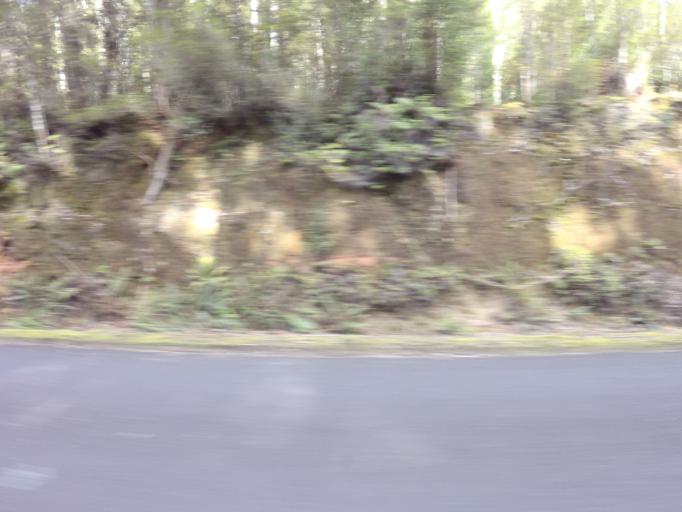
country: AU
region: Tasmania
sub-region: Huon Valley
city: Geeveston
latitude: -42.8249
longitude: 146.3156
